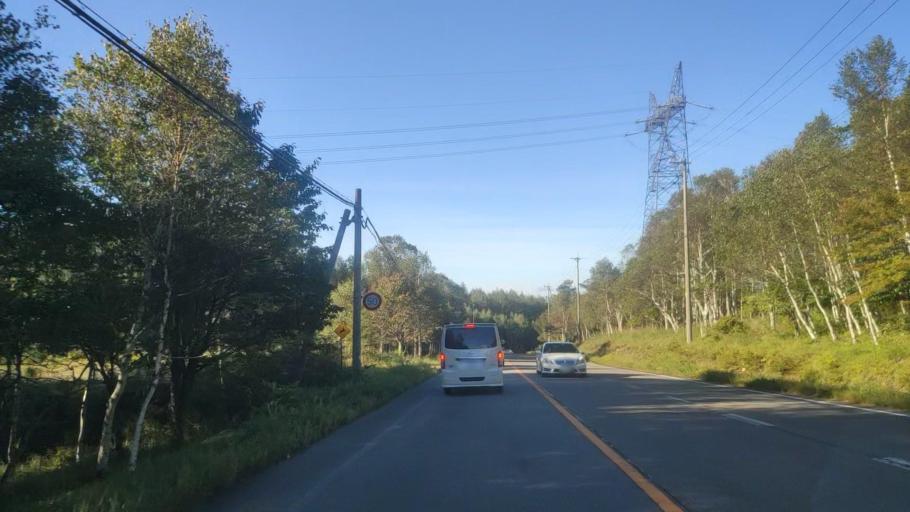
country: JP
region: Nagano
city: Kamimaruko
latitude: 36.1581
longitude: 138.2791
